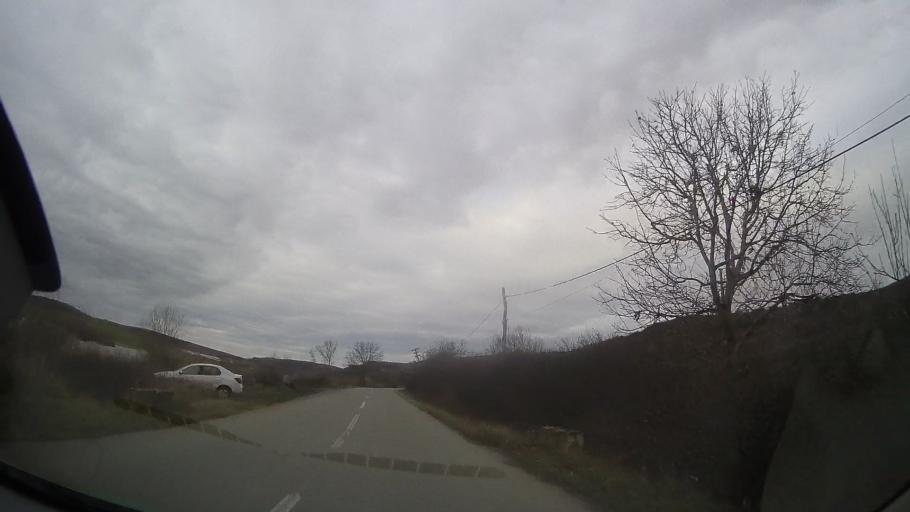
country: RO
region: Mures
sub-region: Comuna Faragau
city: Faragau
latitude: 46.7490
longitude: 24.5283
